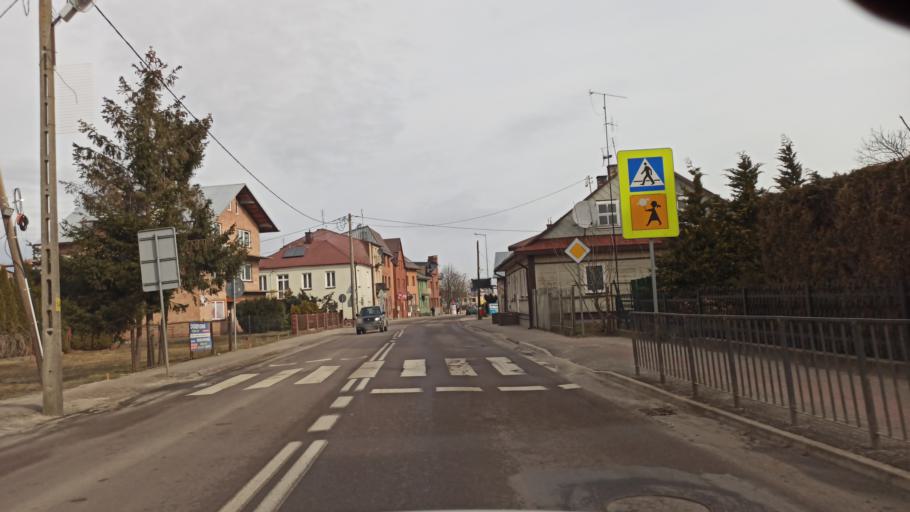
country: PL
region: Lublin Voivodeship
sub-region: Powiat bilgorajski
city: Tarnogrod
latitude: 50.3588
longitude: 22.7410
